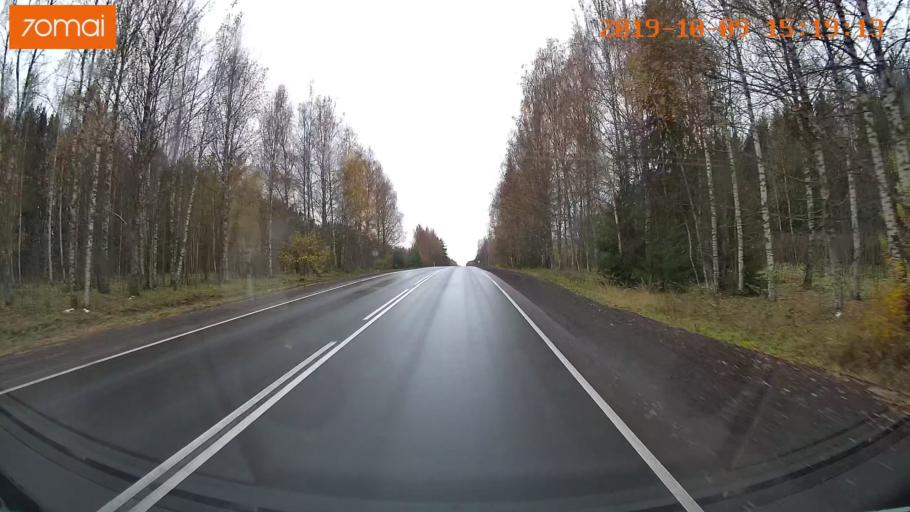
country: RU
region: Kostroma
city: Susanino
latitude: 58.0780
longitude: 41.5602
